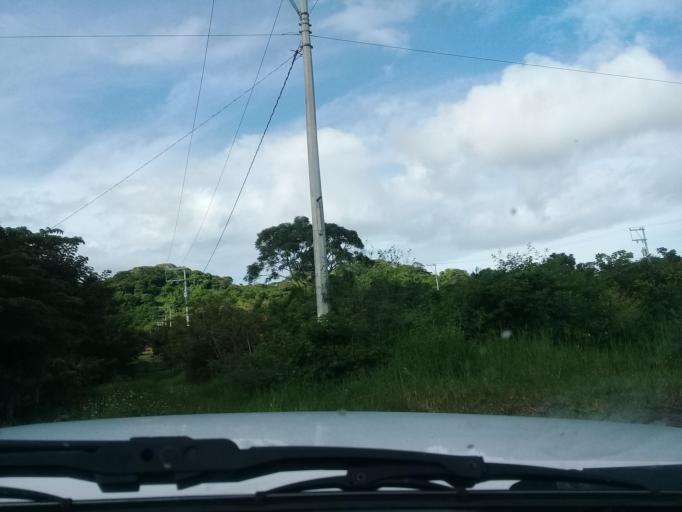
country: MX
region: Veracruz
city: Catemaco
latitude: 18.4348
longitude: -95.1222
